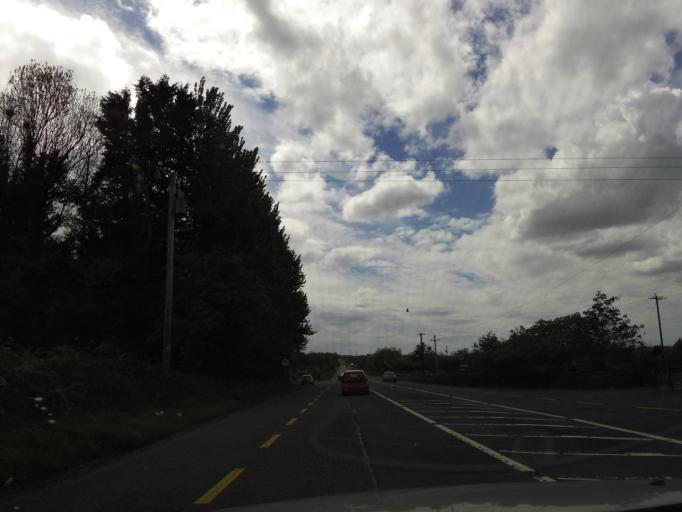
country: IE
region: Connaught
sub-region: County Galway
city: Claregalway
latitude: 53.3279
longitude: -8.9657
